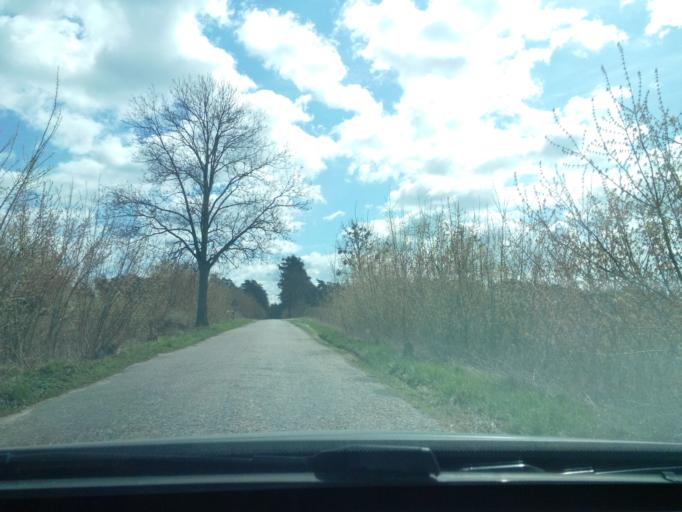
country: PL
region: Warmian-Masurian Voivodeship
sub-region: Powiat nowomiejski
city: Biskupiec
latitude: 53.4575
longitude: 19.2813
